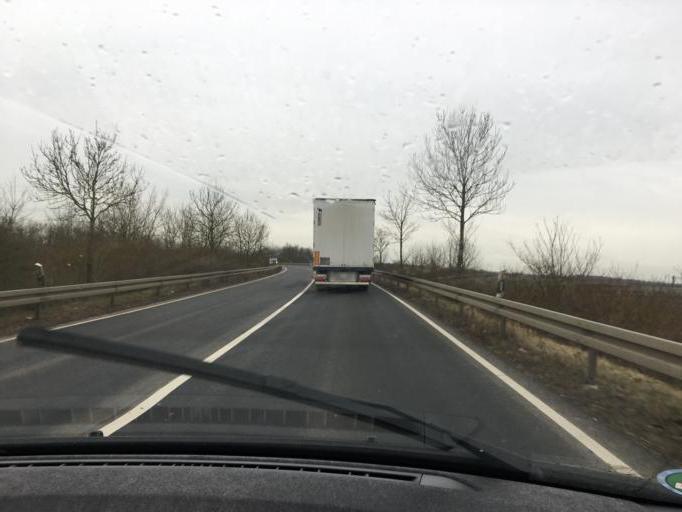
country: DE
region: North Rhine-Westphalia
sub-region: Regierungsbezirk Koln
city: Bergheim
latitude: 50.9221
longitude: 6.6135
